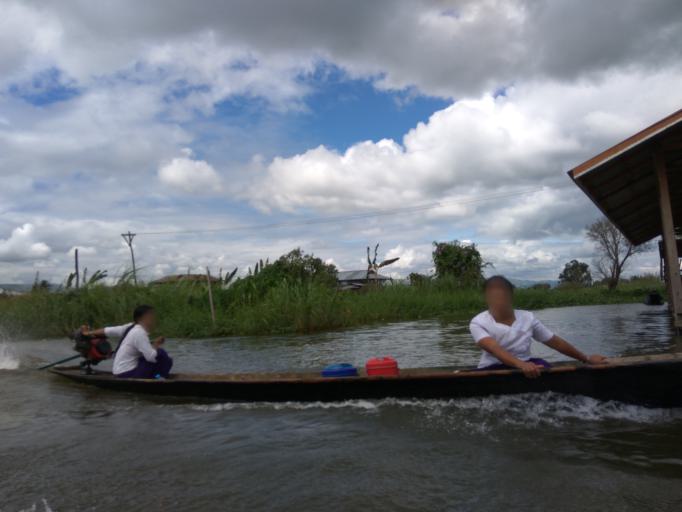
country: MM
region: Shan
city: Taunggyi
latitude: 20.4466
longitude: 96.8999
